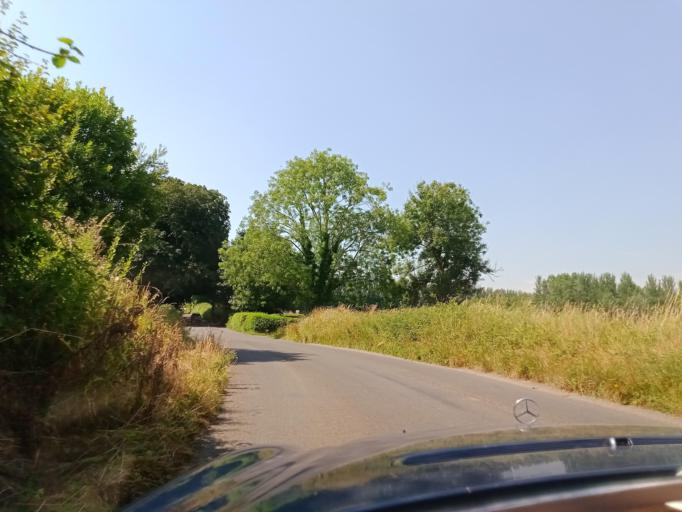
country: IE
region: Leinster
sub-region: Kilkenny
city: Piltown
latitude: 52.3354
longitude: -7.3032
